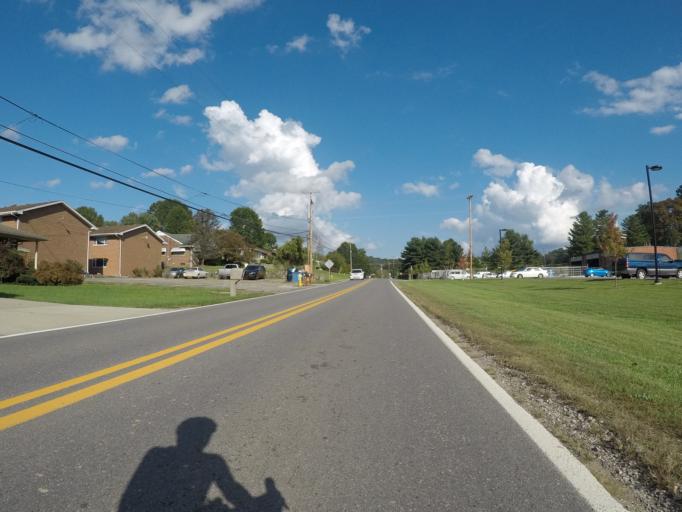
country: US
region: Ohio
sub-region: Lawrence County
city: Burlington
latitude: 38.3839
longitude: -82.5189
